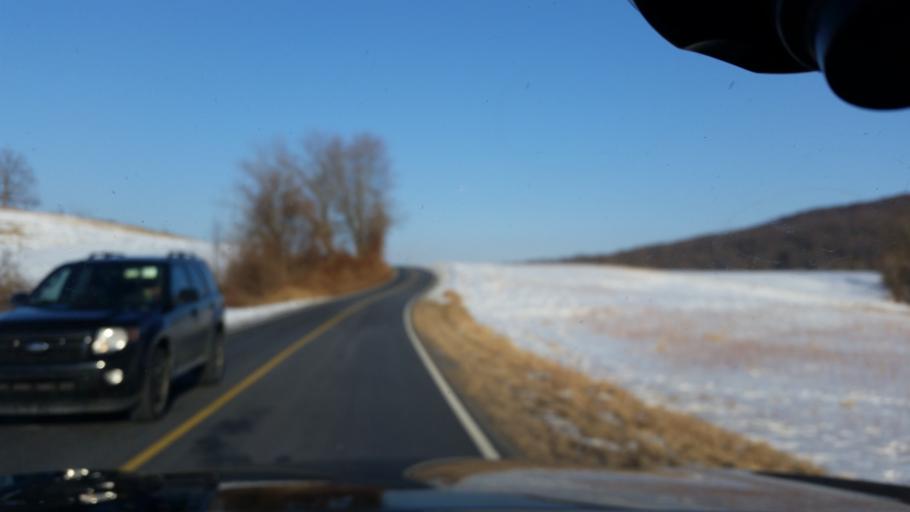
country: US
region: Pennsylvania
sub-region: Perry County
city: Marysville
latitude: 40.3284
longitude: -76.9675
